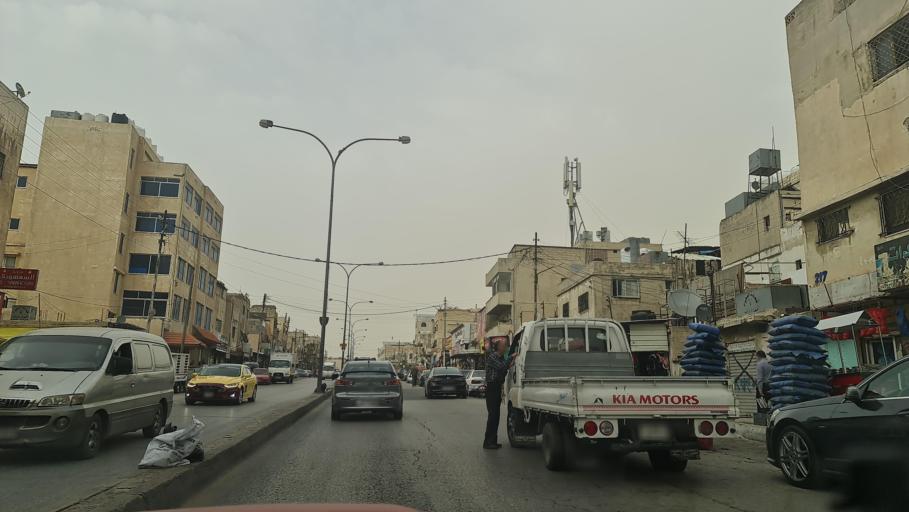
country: JO
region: Amman
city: Al Quwaysimah
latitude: 31.9332
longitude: 35.9348
